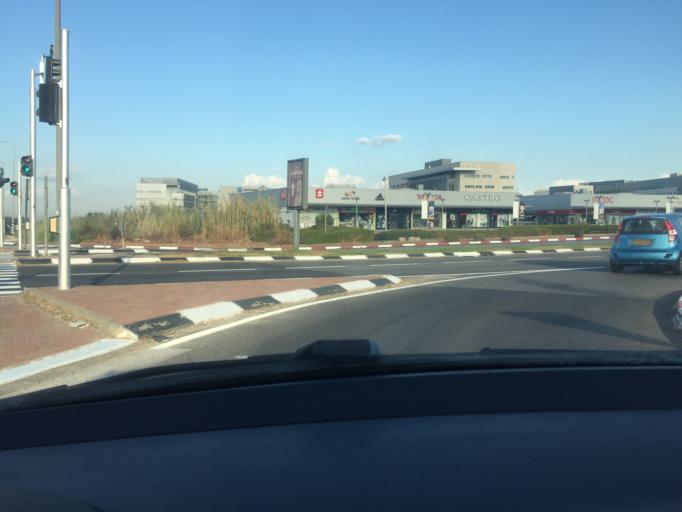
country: IL
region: Central District
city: Lod
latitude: 31.9847
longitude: 34.9153
